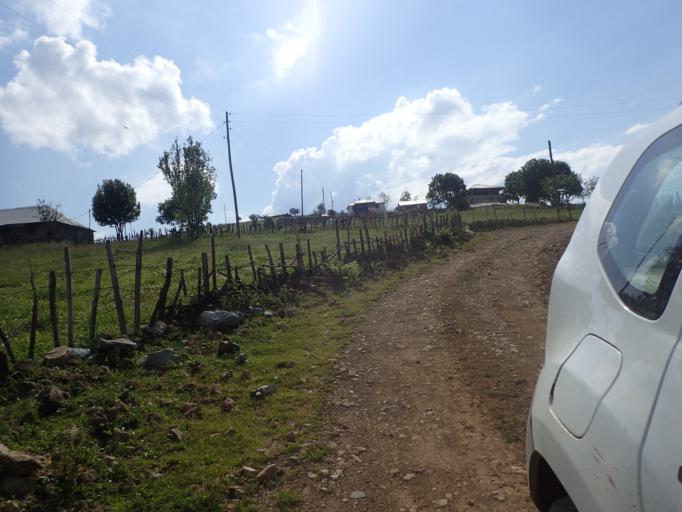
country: TR
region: Ordu
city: Topcam
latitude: 40.6803
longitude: 37.9194
